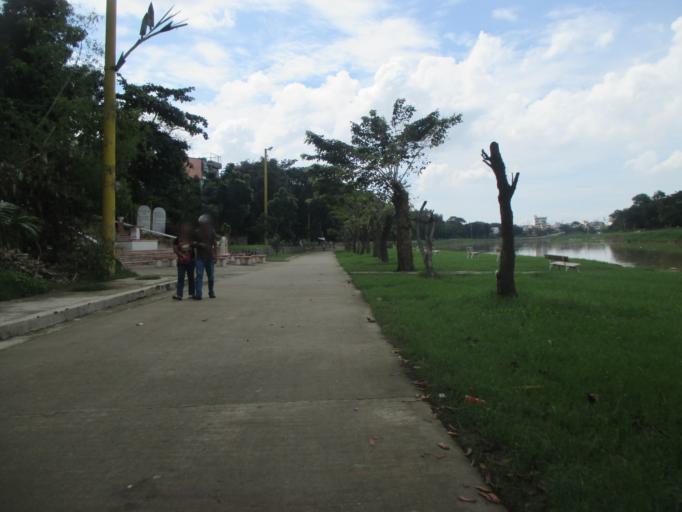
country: PH
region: Metro Manila
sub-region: Marikina
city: Calumpang
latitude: 14.6302
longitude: 121.0944
